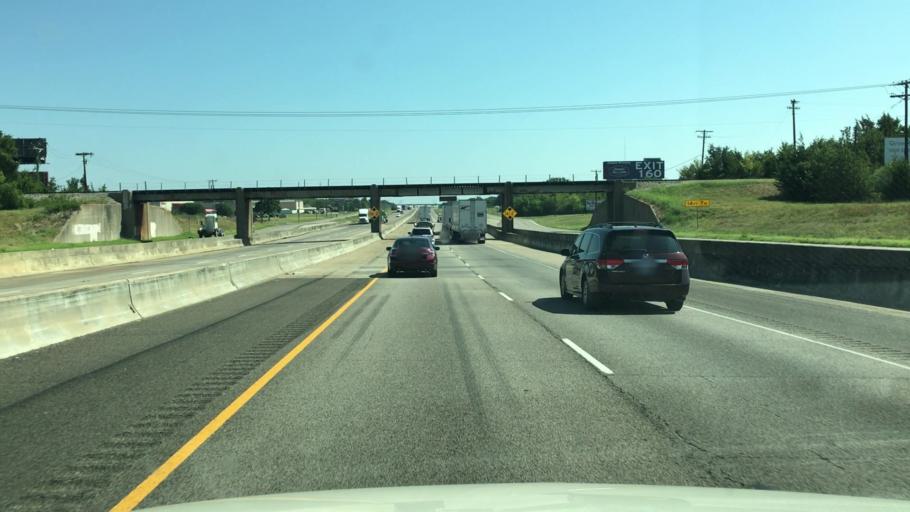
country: US
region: Texas
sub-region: Hopkins County
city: Sulphur Springs
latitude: 33.1254
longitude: -95.5812
